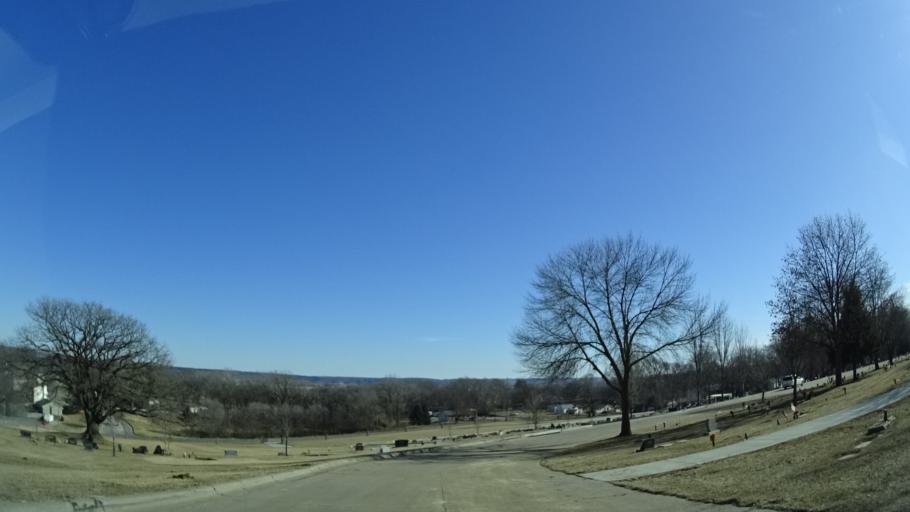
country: US
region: Nebraska
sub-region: Sarpy County
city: Bellevue
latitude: 41.1499
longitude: -95.8929
